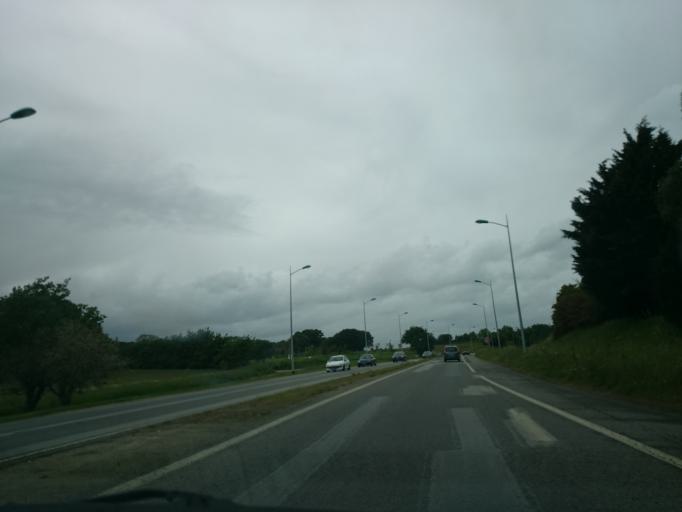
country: FR
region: Brittany
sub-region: Departement du Morbihan
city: Vannes
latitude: 47.6718
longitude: -2.7721
